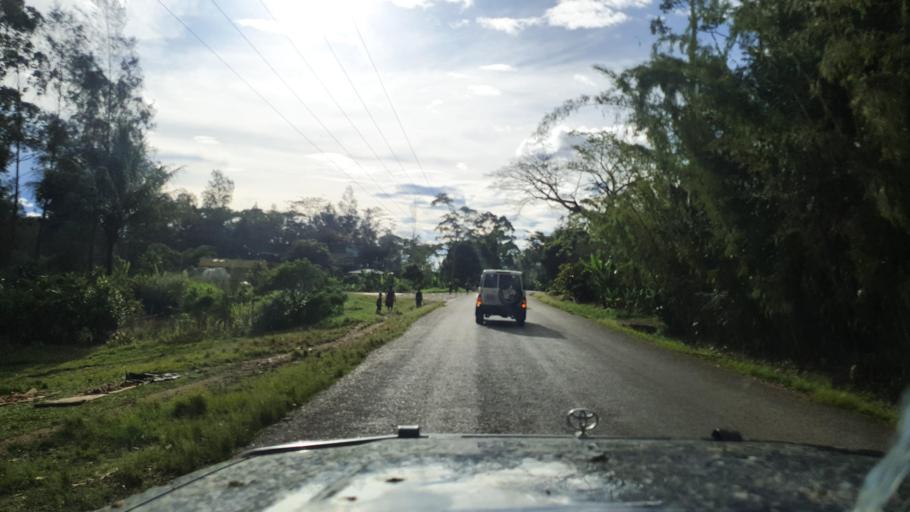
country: PG
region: Jiwaka
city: Minj
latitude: -5.9004
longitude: 144.7468
